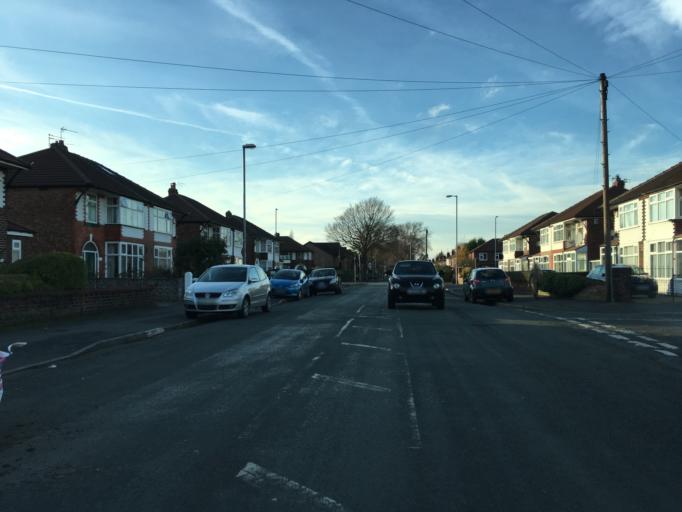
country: GB
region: England
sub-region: Manchester
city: Chorlton cum Hardy
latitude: 53.4459
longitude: -2.2665
